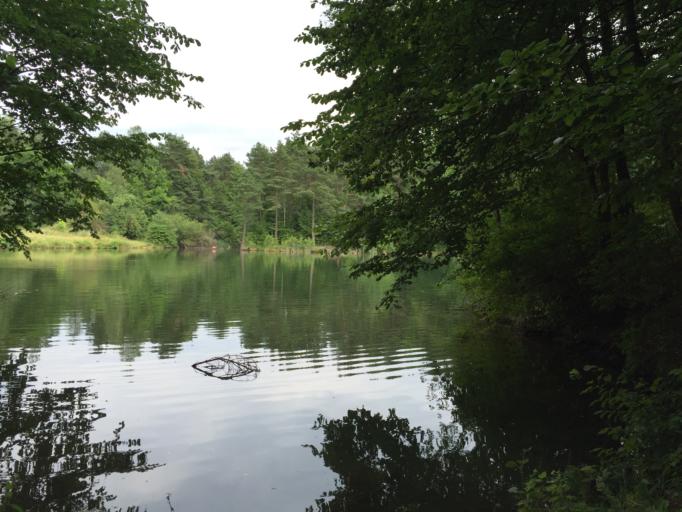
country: PL
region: Lesser Poland Voivodeship
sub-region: Powiat olkuski
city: Klucze
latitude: 50.3415
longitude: 19.5501
